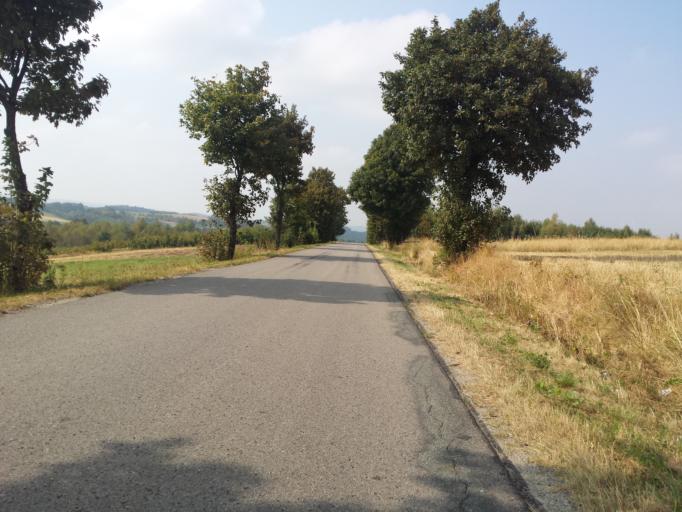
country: PL
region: Subcarpathian Voivodeship
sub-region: Powiat brzozowski
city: Wesola
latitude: 49.8418
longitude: 22.1500
